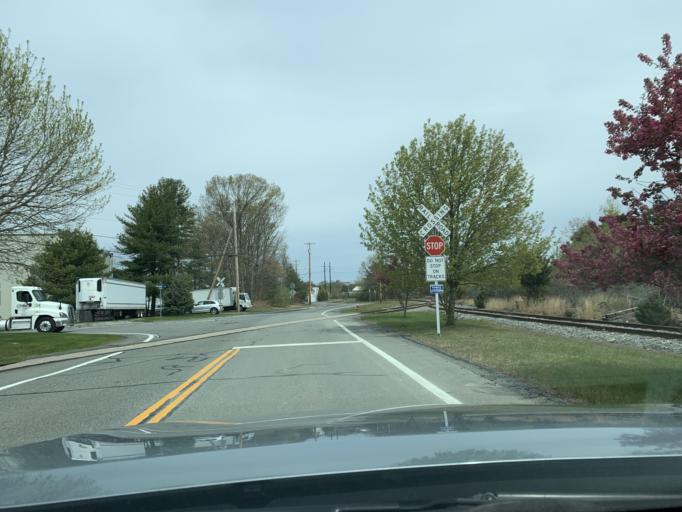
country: US
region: Rhode Island
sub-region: Washington County
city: North Kingstown
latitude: 41.6034
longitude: -71.4703
